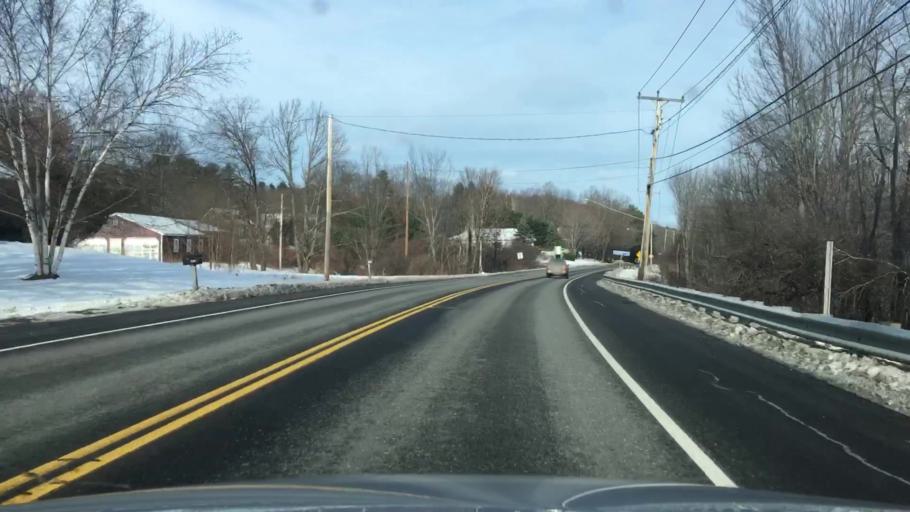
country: US
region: Maine
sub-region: Androscoggin County
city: Lewiston
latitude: 44.1491
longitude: -70.1910
